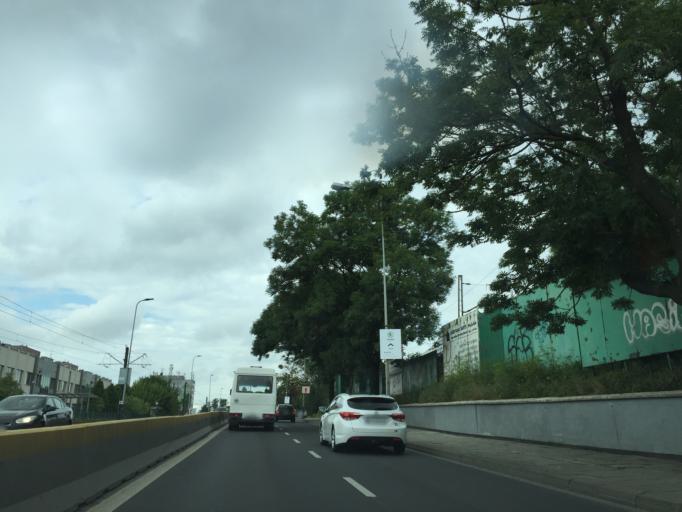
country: PL
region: Lesser Poland Voivodeship
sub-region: Krakow
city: Krakow
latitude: 50.0234
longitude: 19.9335
